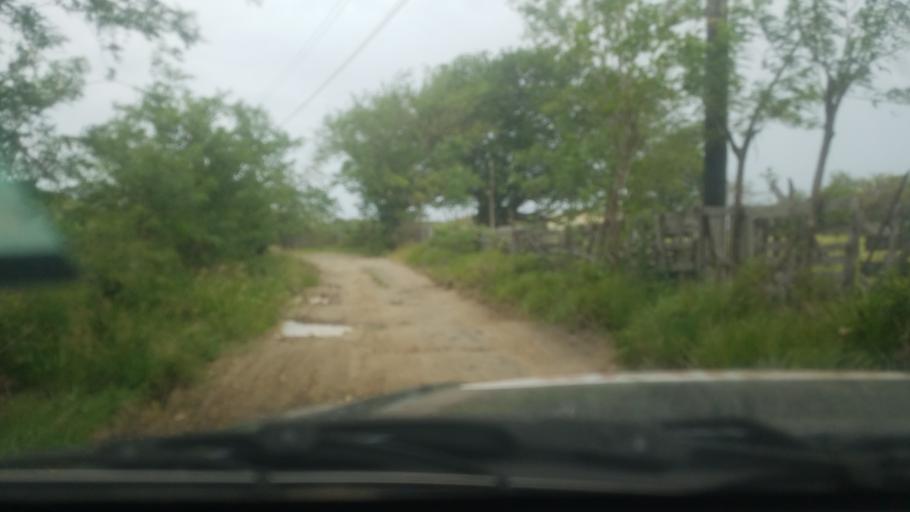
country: LC
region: Laborie Quarter
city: Laborie
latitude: 13.7451
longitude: -60.9785
